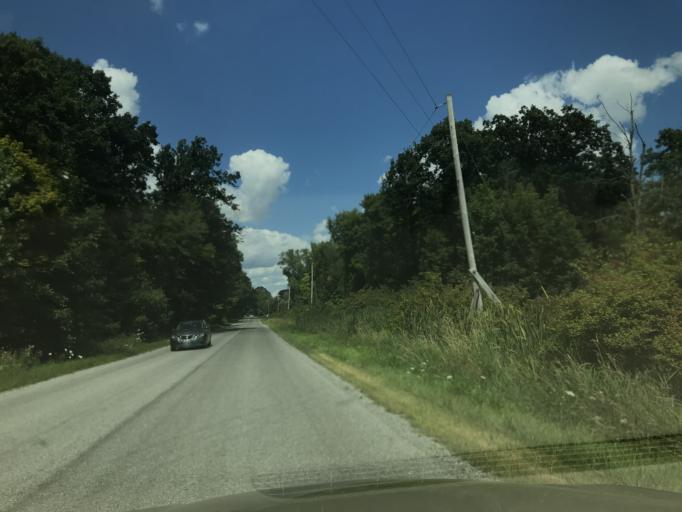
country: US
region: Michigan
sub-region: Ingham County
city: Holt
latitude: 42.6185
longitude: -84.5626
